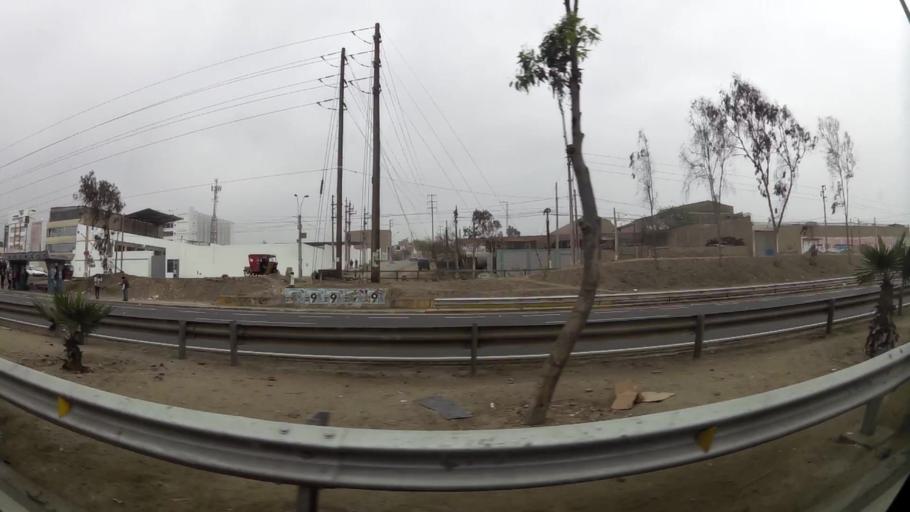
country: PE
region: Lima
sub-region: Lima
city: Surco
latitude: -12.1970
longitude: -76.9732
